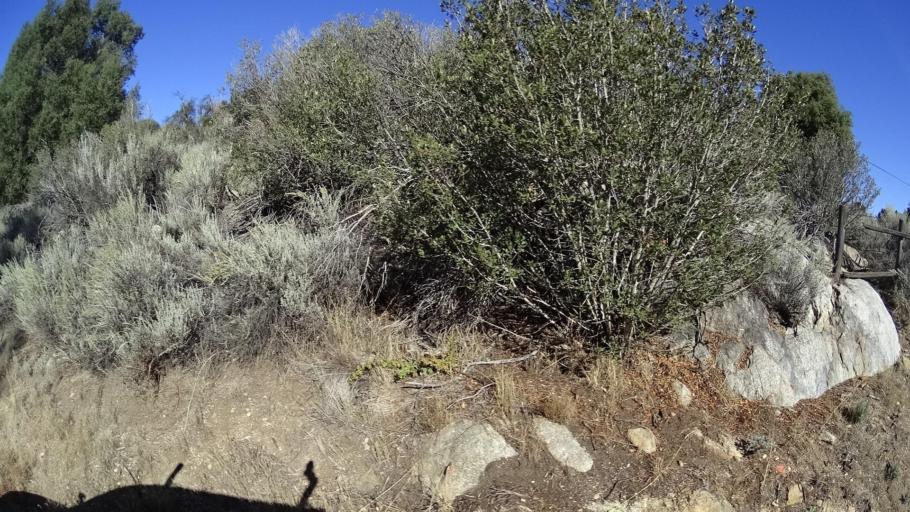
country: US
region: California
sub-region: San Diego County
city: Pine Valley
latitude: 32.8381
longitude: -116.5347
